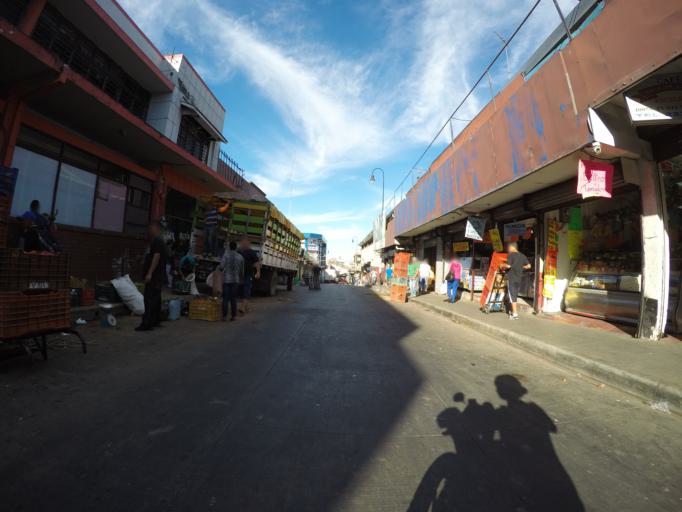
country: CR
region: San Jose
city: San Jose
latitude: 9.9360
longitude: -84.0826
